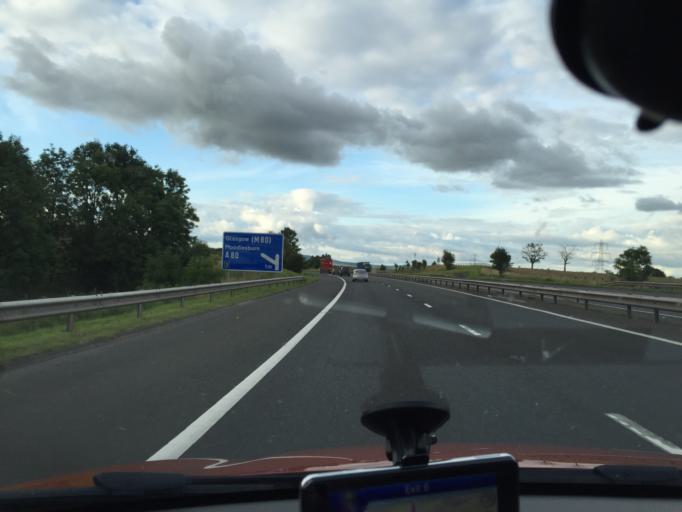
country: GB
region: Scotland
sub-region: North Lanarkshire
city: Glenboig
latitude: 55.8967
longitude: -4.0683
